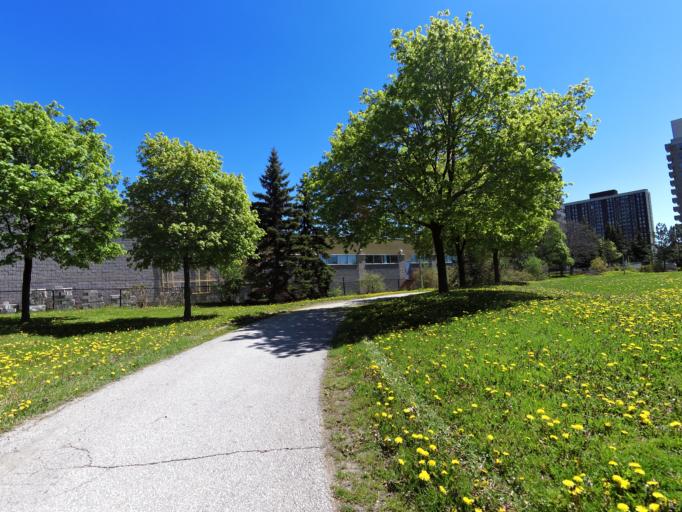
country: CA
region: Ontario
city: Brampton
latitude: 43.7199
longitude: -79.7184
